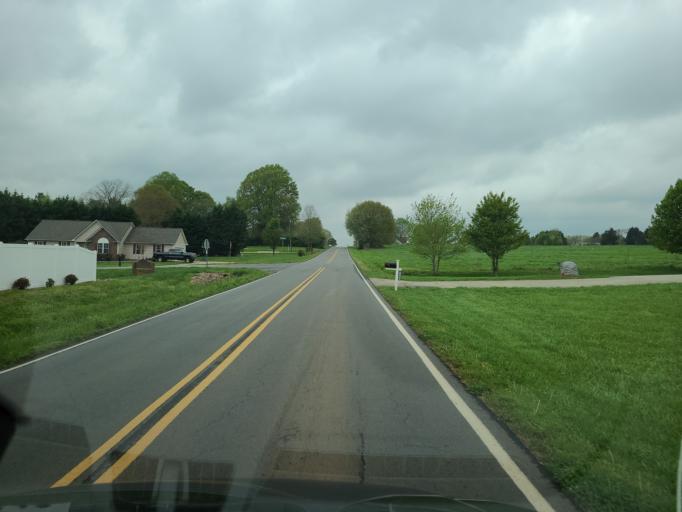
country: US
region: North Carolina
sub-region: Lincoln County
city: Lincolnton
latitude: 35.4607
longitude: -81.3225
